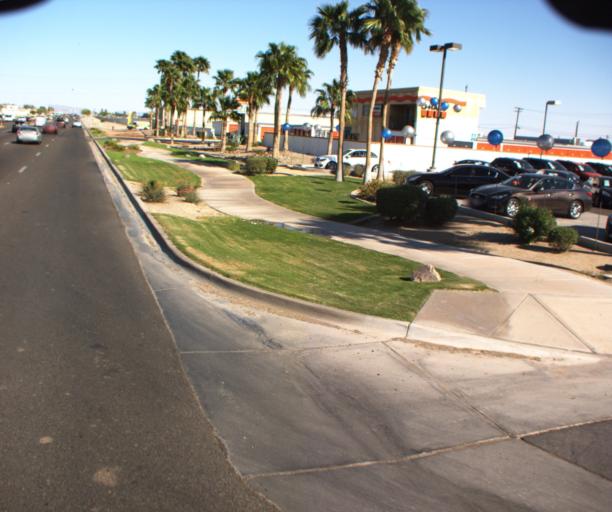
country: US
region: Arizona
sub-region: Yuma County
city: Yuma
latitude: 32.6693
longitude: -114.6087
